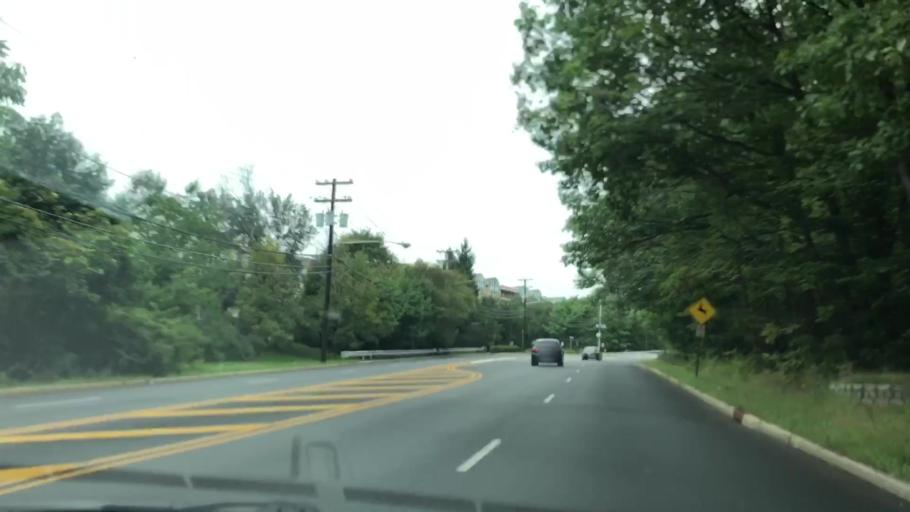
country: US
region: New Jersey
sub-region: Essex County
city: West Orange
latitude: 40.7997
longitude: -74.2399
